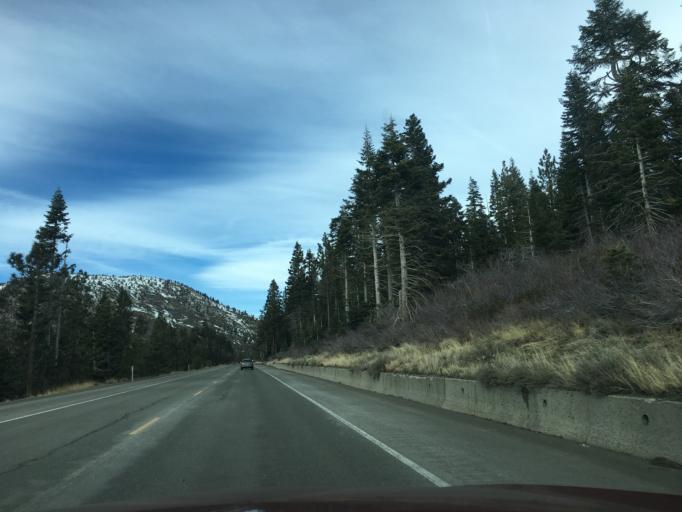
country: US
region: Nevada
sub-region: Washoe County
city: Incline Village
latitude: 39.2734
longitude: -119.9332
